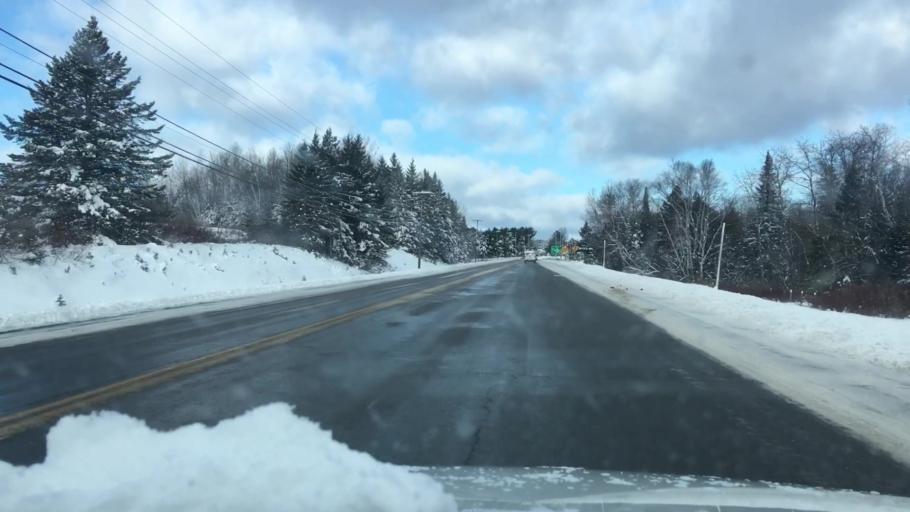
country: US
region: Maine
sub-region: Aroostook County
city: Caribou
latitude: 46.8760
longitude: -68.0066
